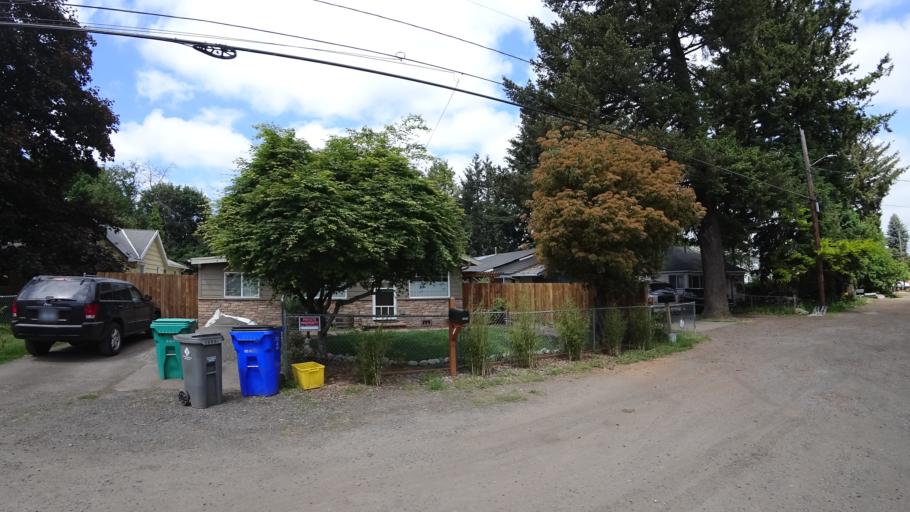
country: US
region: Oregon
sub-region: Multnomah County
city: Gresham
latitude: 45.5021
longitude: -122.4911
